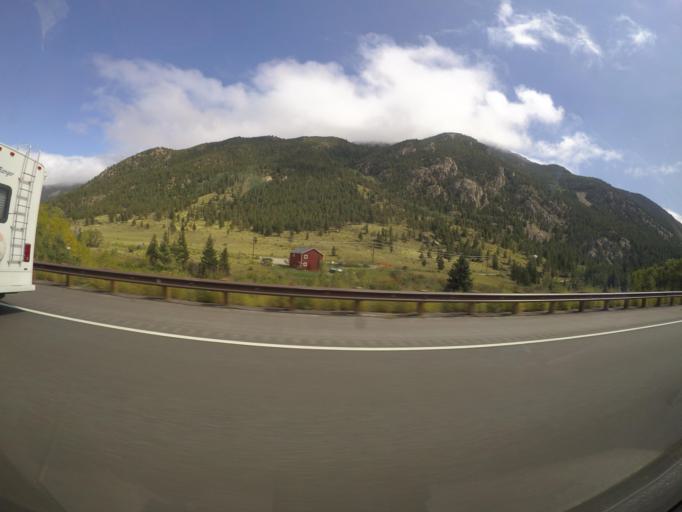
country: US
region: Colorado
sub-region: Clear Creek County
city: Georgetown
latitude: 39.7386
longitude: -105.6873
